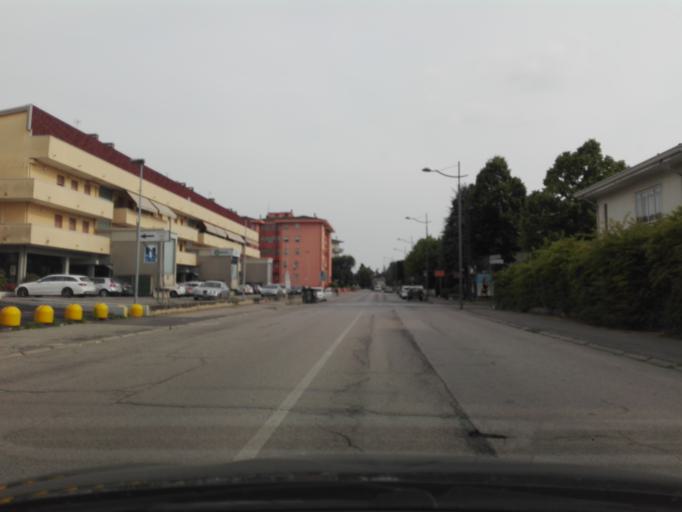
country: IT
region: Veneto
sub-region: Provincia di Rovigo
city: Rovigo
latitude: 45.0775
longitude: 11.7979
